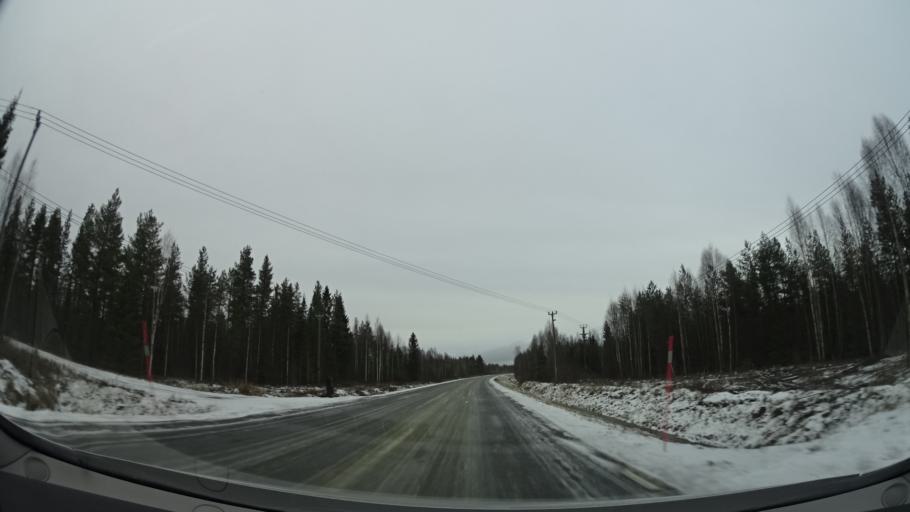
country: SE
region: Vaesterbotten
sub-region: Lycksele Kommun
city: Lycksele
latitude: 64.5529
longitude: 18.5116
